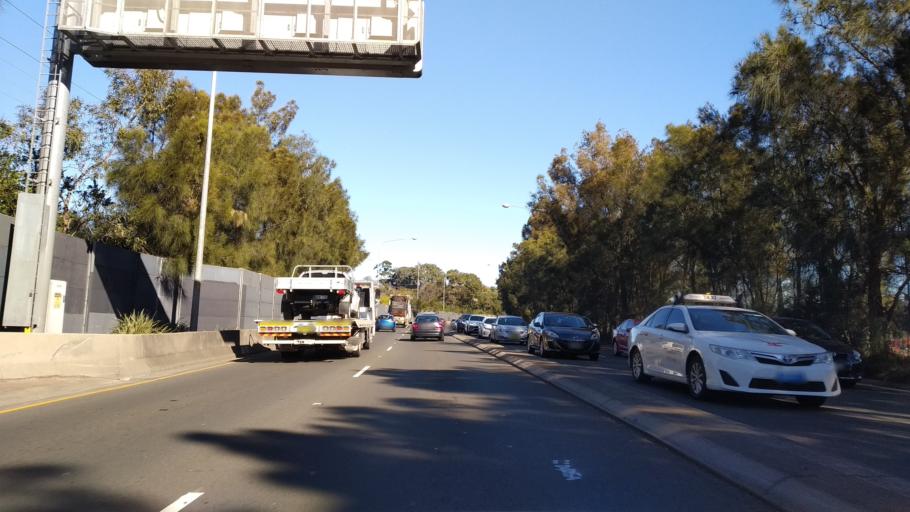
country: AU
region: New South Wales
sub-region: Leichhardt
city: Lilyfield
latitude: -33.8726
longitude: 151.1704
